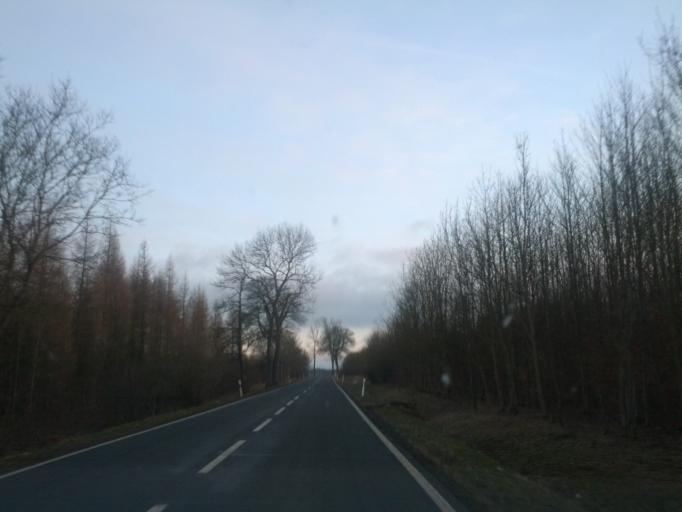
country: DE
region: Thuringia
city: Heyerode
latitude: 51.1935
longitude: 10.2983
